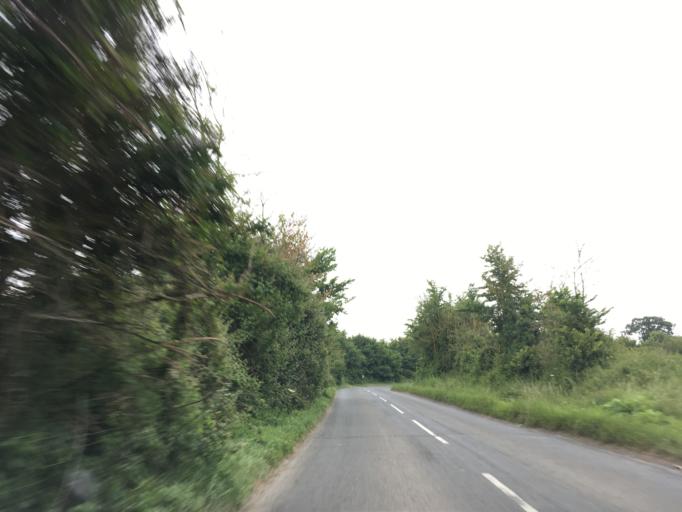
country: GB
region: England
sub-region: Gloucestershire
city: Stonehouse
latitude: 51.7800
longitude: -2.3468
